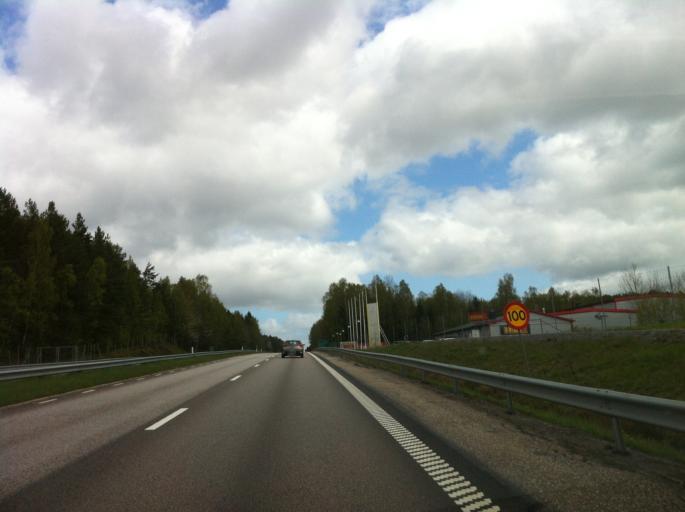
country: SE
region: Vaestra Goetaland
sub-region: Alingsas Kommun
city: Ingared
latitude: 57.8503
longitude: 12.4714
